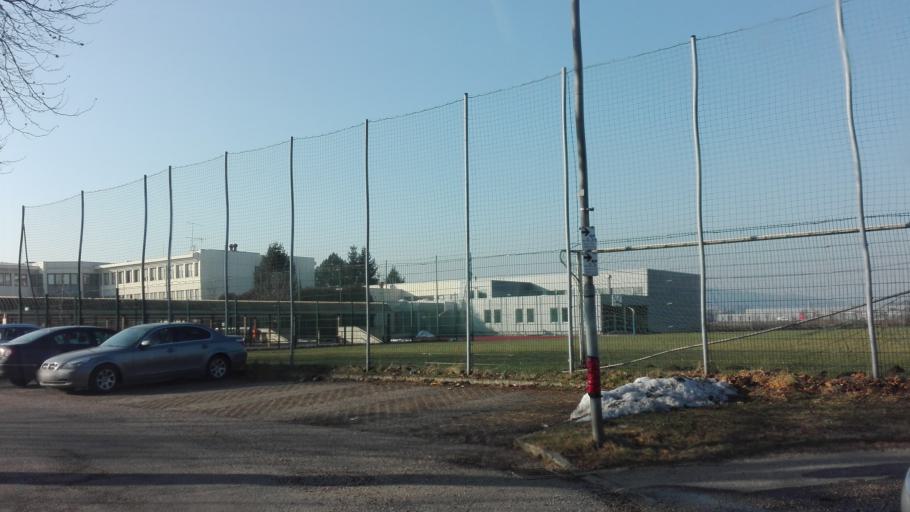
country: AT
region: Upper Austria
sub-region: Politischer Bezirk Linz-Land
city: Leonding
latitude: 48.2680
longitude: 14.2539
